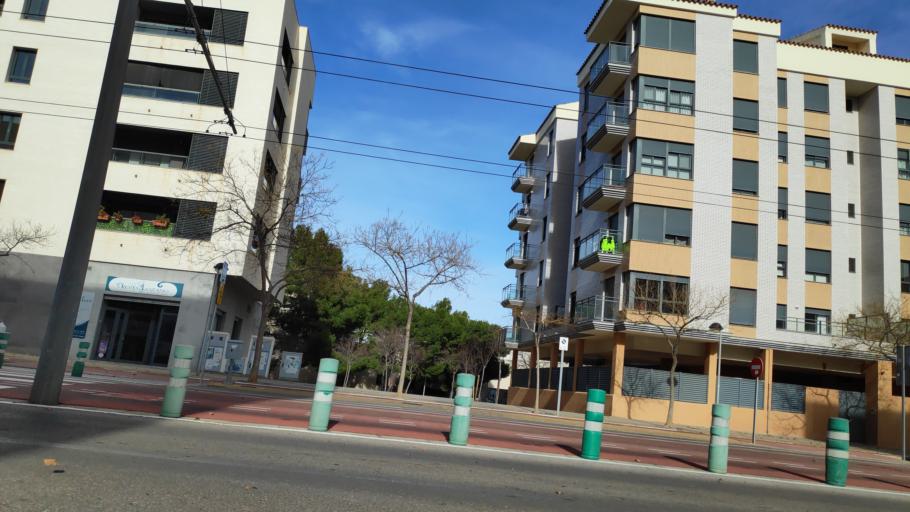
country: ES
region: Valencia
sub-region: Provincia de Castello
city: Castello de la Plana
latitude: 39.9917
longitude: -0.0596
